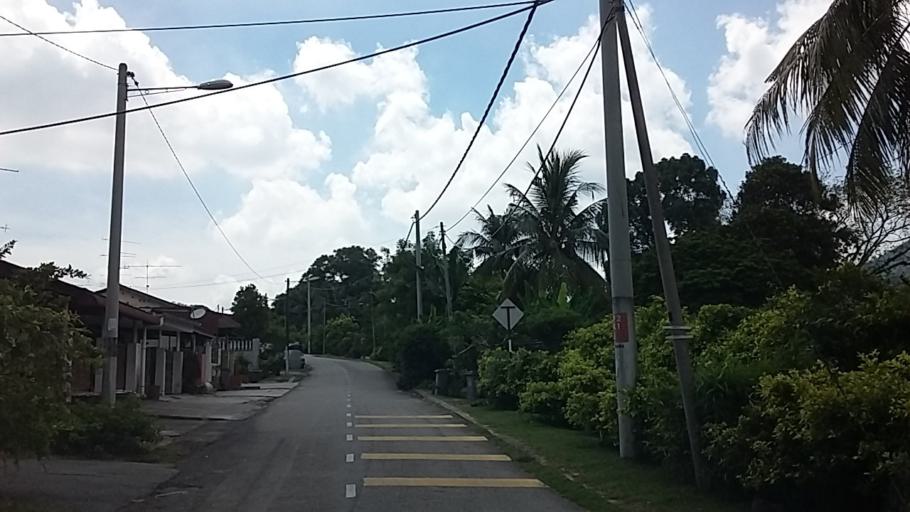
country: MY
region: Johor
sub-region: Daerah Batu Pahat
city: Batu Pahat
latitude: 1.8423
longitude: 102.9451
